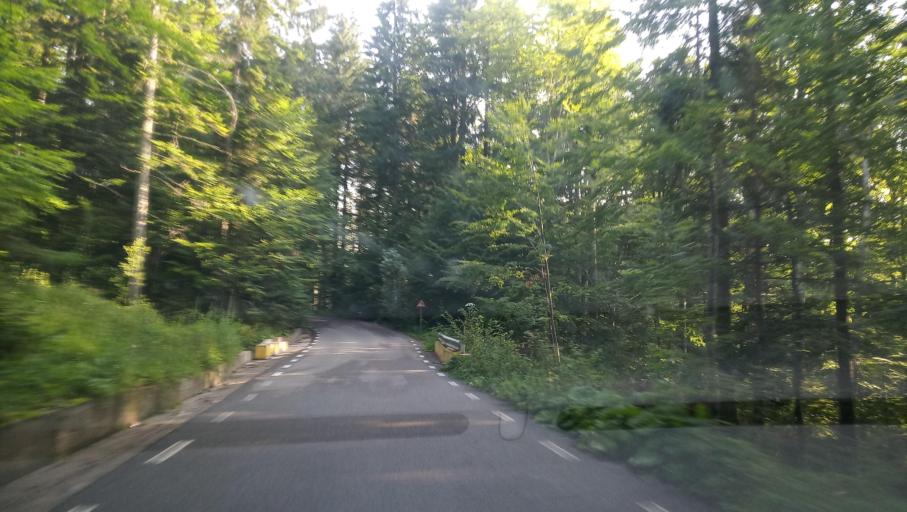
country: RO
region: Prahova
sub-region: Oras Sinaia
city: Sinaia
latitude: 45.3120
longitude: 25.5202
